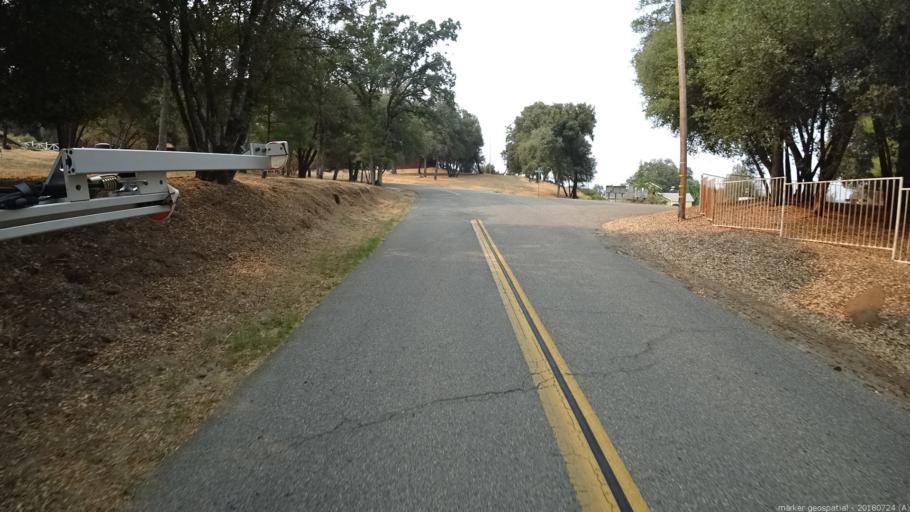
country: US
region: California
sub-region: Madera County
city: Oakhurst
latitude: 37.3221
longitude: -119.6172
